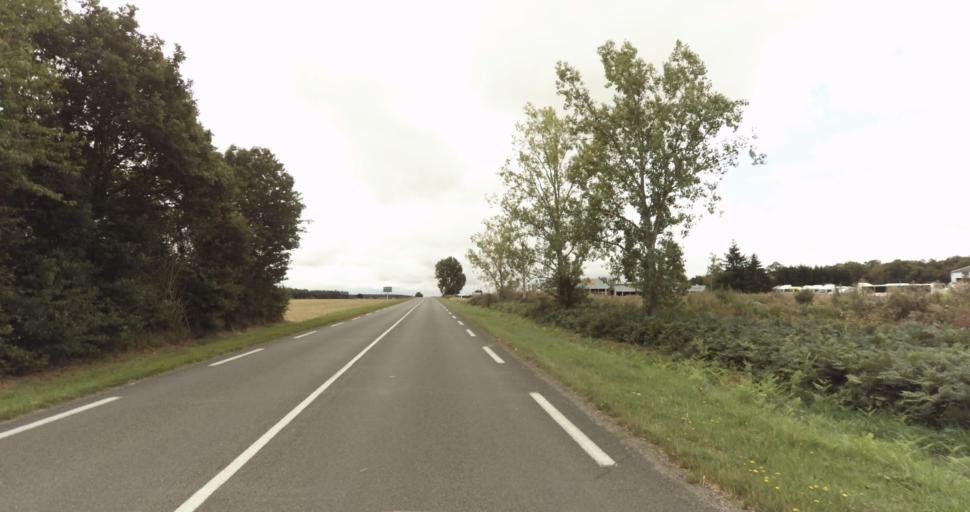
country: FR
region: Haute-Normandie
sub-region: Departement de l'Eure
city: Evreux
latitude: 48.9610
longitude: 1.1610
